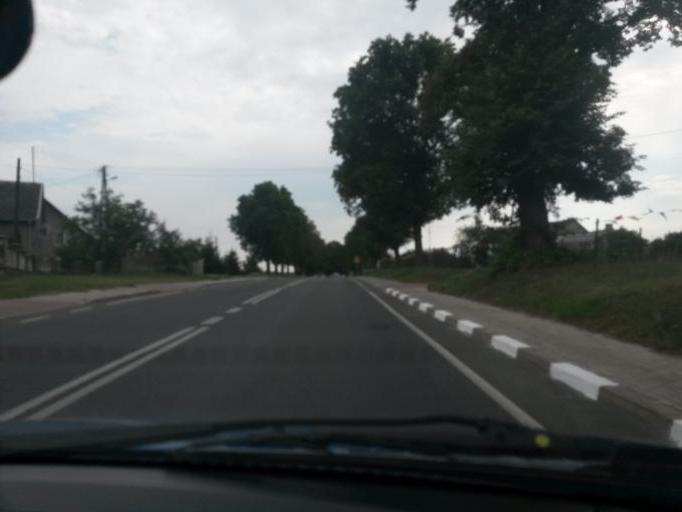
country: PL
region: Masovian Voivodeship
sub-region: Powiat zurominski
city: Lubowidz
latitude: 53.1166
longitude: 19.8462
